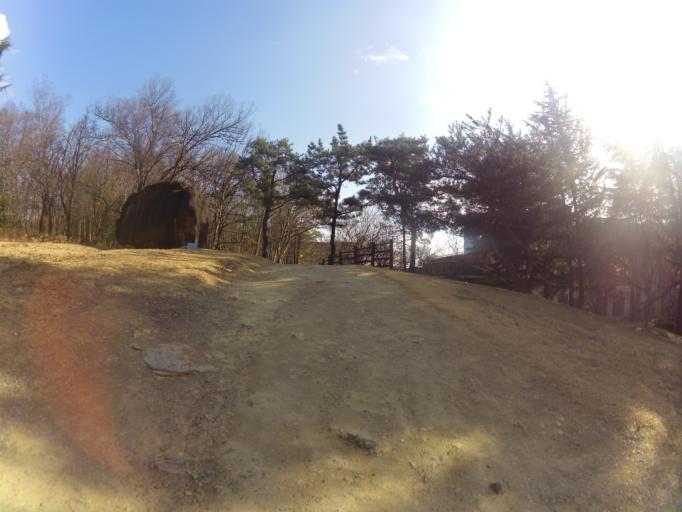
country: KR
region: Gyeongsangbuk-do
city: Gyeongsan-si
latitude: 35.8359
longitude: 128.7560
